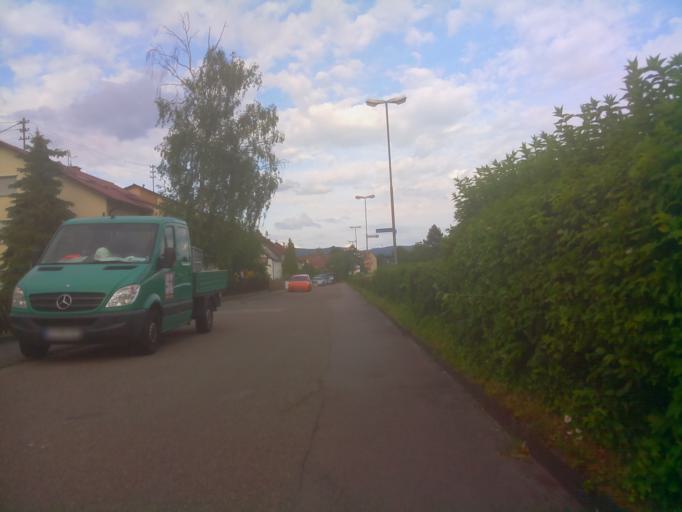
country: DE
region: Baden-Wuerttemberg
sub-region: Karlsruhe Region
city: Ladenburg
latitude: 49.4696
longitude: 8.5946
